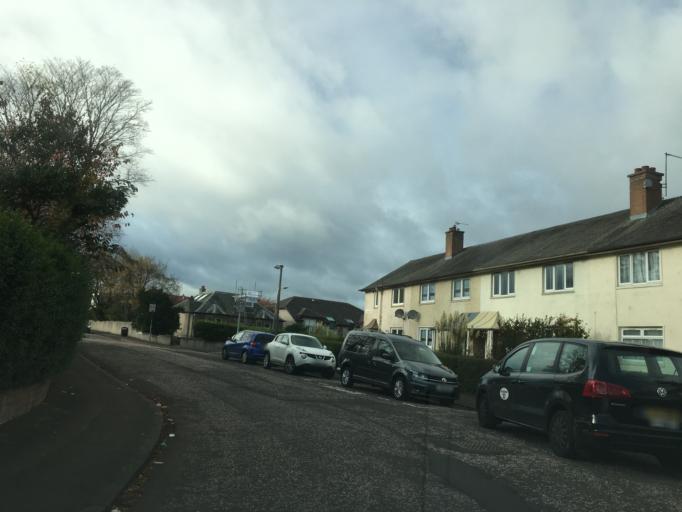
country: GB
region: Scotland
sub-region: Midlothian
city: Loanhead
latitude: 55.9155
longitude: -3.1616
